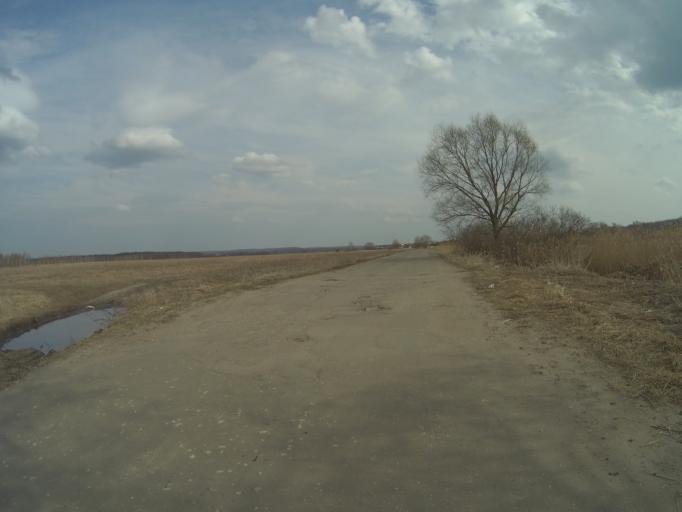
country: RU
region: Vladimir
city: Raduzhnyy
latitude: 56.0184
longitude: 40.3524
